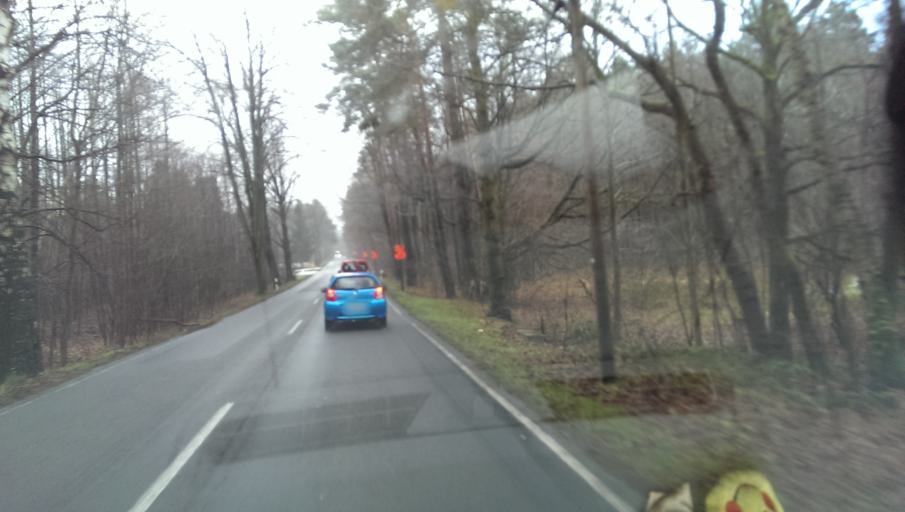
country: DE
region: Saxony
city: Weinbohla
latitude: 51.1978
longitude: 13.5956
